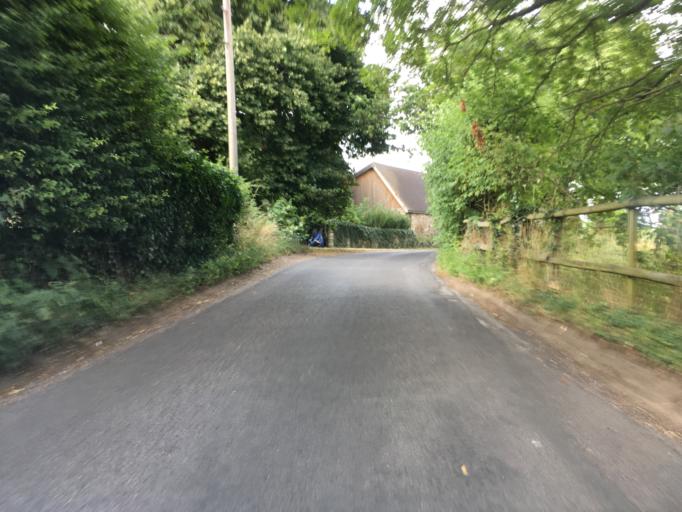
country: GB
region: England
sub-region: Kent
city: Maidstone
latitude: 51.2465
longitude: 0.5121
